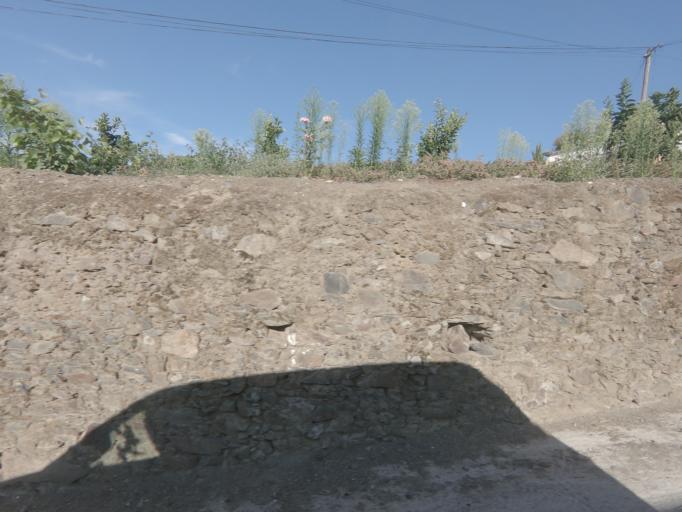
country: PT
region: Vila Real
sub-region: Santa Marta de Penaguiao
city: Santa Marta de Penaguiao
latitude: 41.1942
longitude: -7.7728
